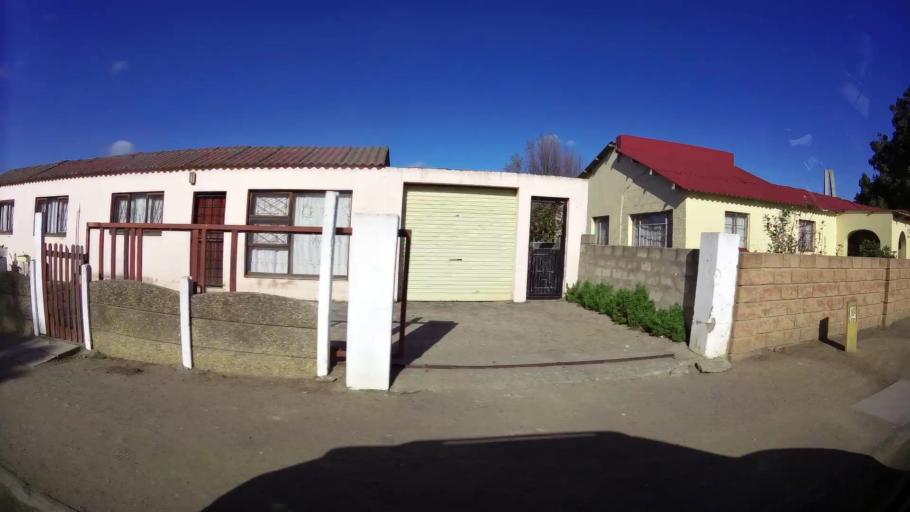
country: ZA
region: Western Cape
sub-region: Eden District Municipality
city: George
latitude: -33.9720
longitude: 22.4791
